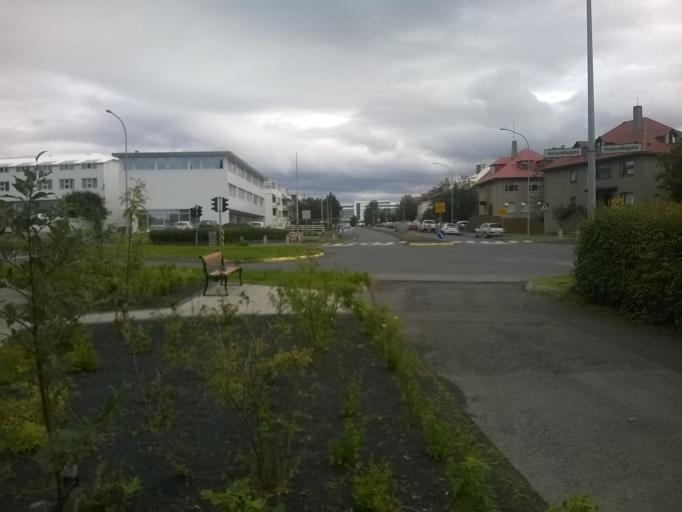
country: IS
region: Capital Region
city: Seltjarnarnes
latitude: 64.1435
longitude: -21.9641
